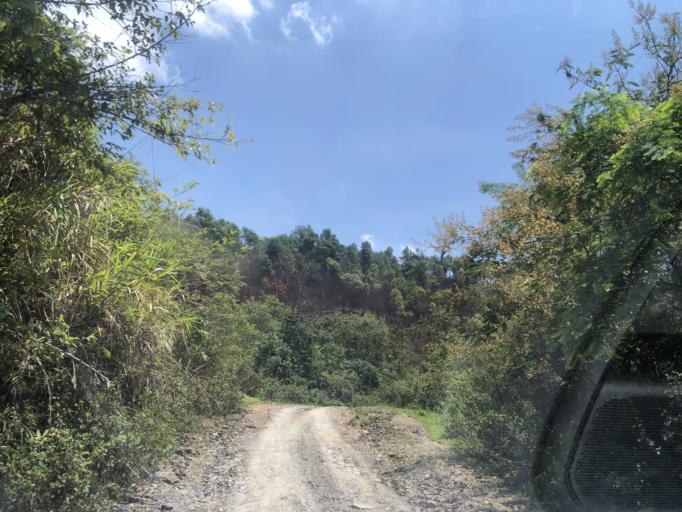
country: LA
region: Phongsali
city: Phongsali
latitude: 21.4409
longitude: 102.1633
